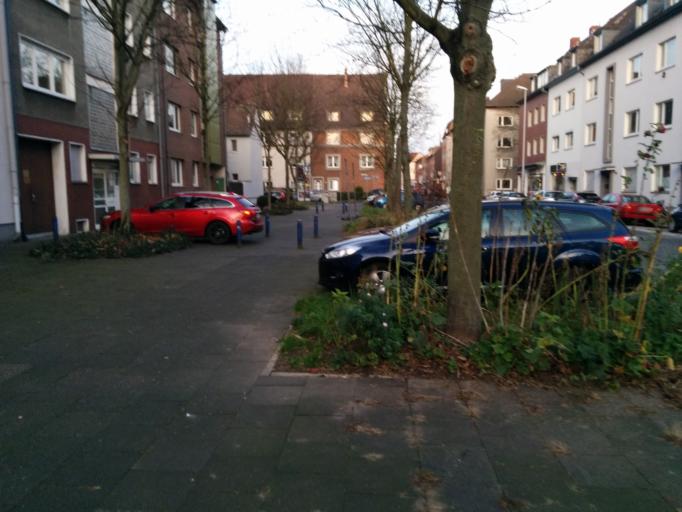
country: DE
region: North Rhine-Westphalia
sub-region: Regierungsbezirk Dusseldorf
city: Duisburg
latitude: 51.4259
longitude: 6.7868
